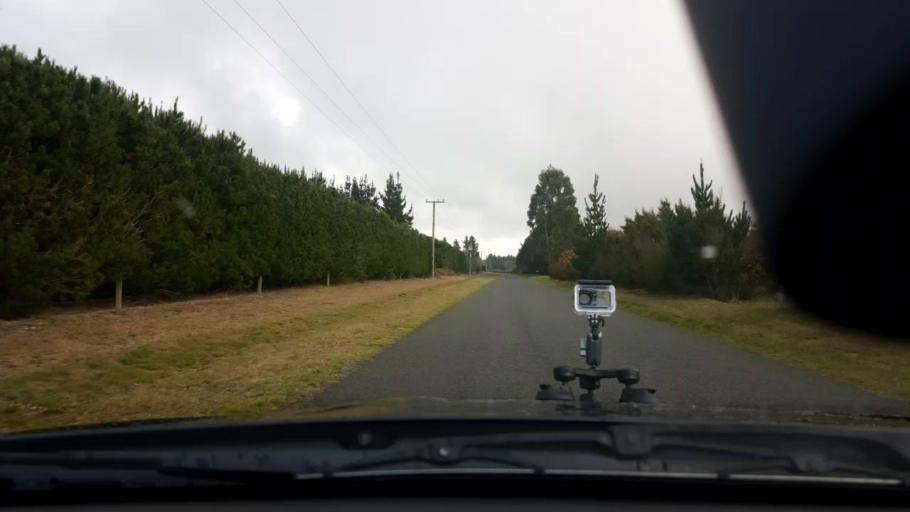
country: NZ
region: Canterbury
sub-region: Waimakariri District
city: Oxford
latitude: -43.3980
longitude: 172.3113
